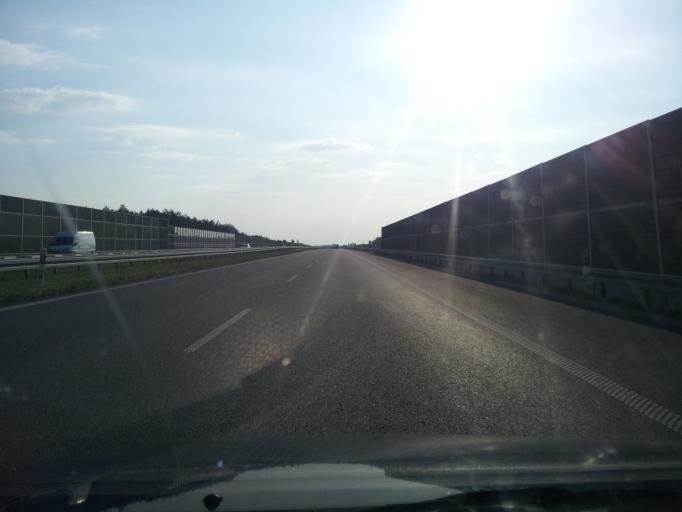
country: PL
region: Lodz Voivodeship
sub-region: powiat Lowicki
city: Bobrowniki
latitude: 52.0379
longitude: 20.0271
